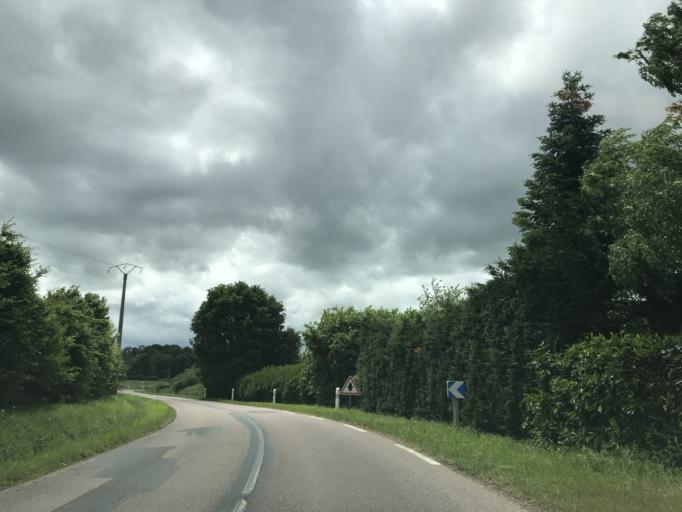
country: FR
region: Ile-de-France
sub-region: Departement des Yvelines
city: Breval
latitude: 48.9653
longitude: 1.5583
